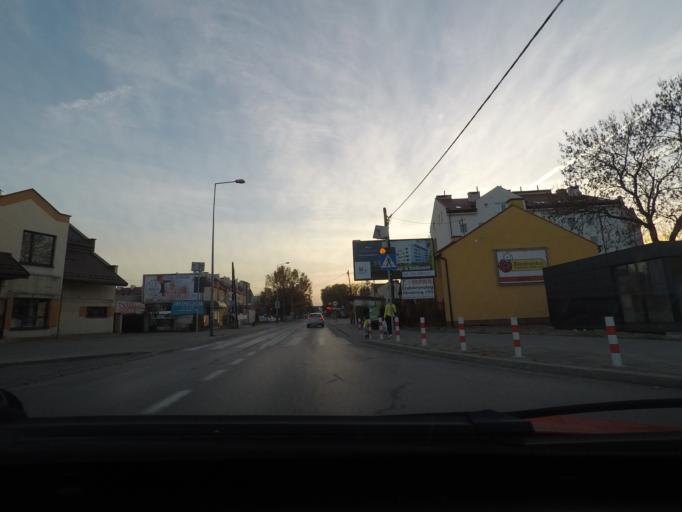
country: PL
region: Lesser Poland Voivodeship
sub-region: Krakow
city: Krakow
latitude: 50.0239
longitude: 19.9109
